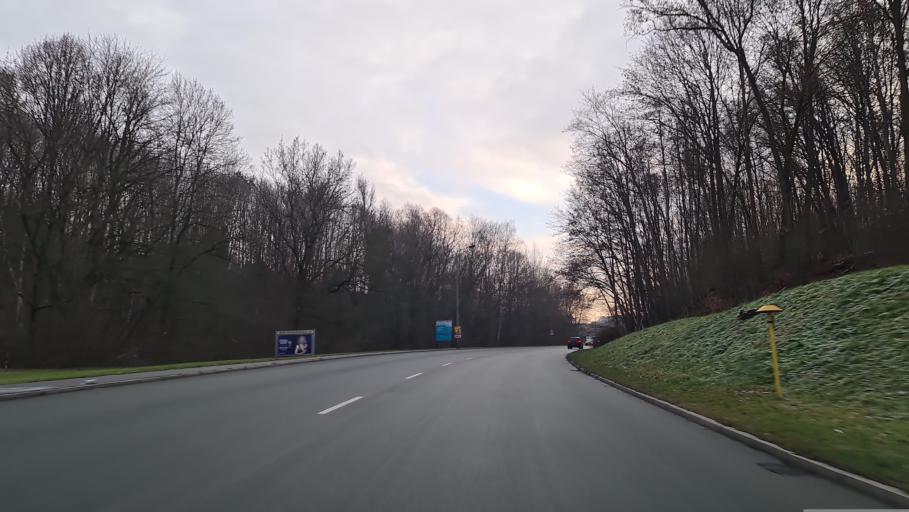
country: DE
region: Saxony
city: Netzschkau
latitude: 50.6185
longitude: 12.2541
